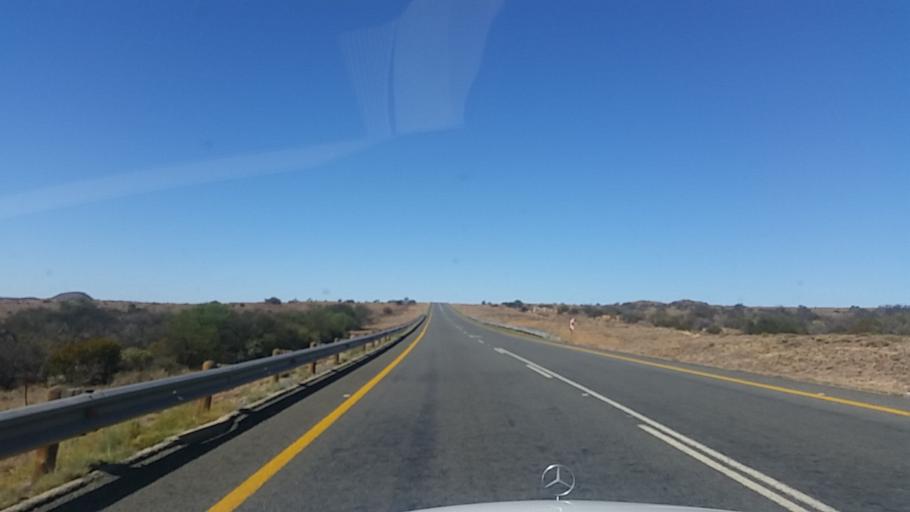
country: ZA
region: Eastern Cape
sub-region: Cacadu District Municipality
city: Graaff-Reinet
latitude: -32.0413
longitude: 24.6188
